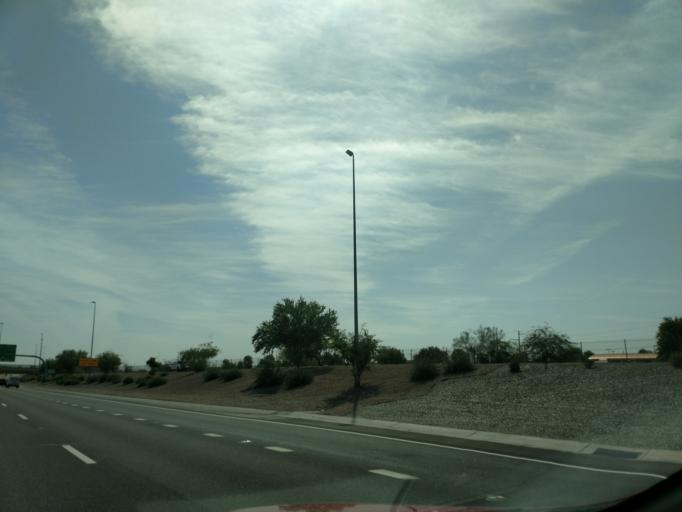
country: US
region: Arizona
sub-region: Maricopa County
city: Guadalupe
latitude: 33.2924
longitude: -111.9838
